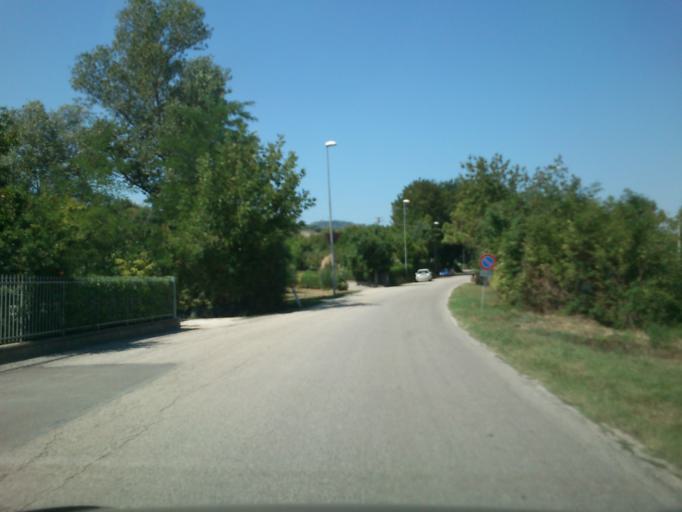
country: IT
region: The Marches
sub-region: Provincia di Pesaro e Urbino
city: Calcinelli
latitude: 43.7756
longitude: 12.9105
